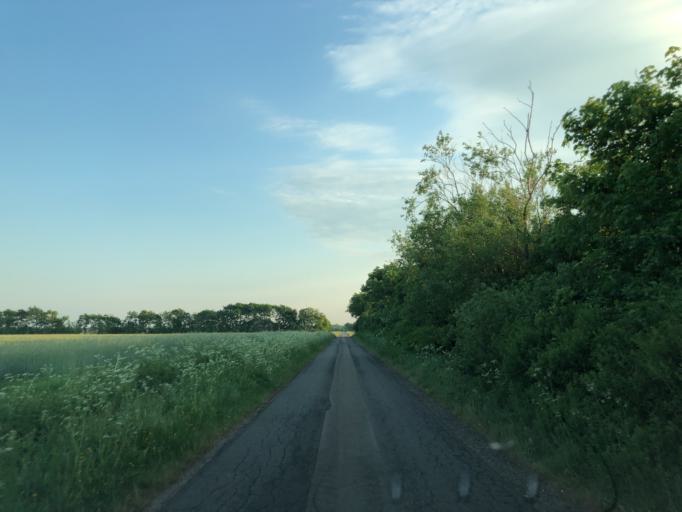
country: DK
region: Central Jutland
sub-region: Holstebro Kommune
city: Holstebro
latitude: 56.3848
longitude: 8.4683
